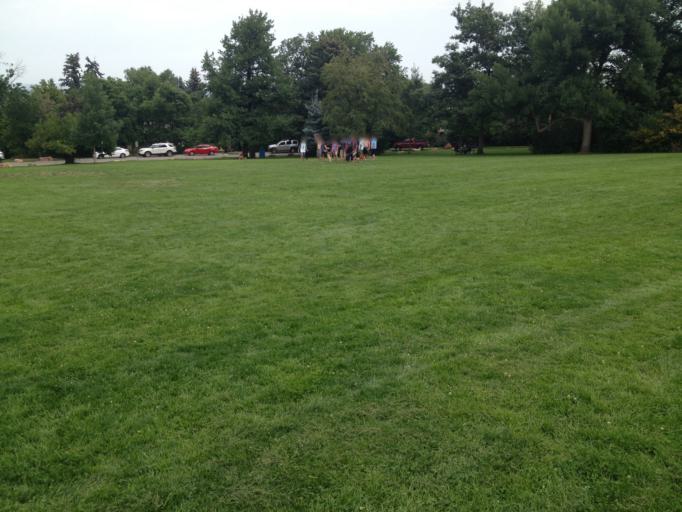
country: US
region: Colorado
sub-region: Boulder County
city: Boulder
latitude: 39.9989
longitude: -105.2813
